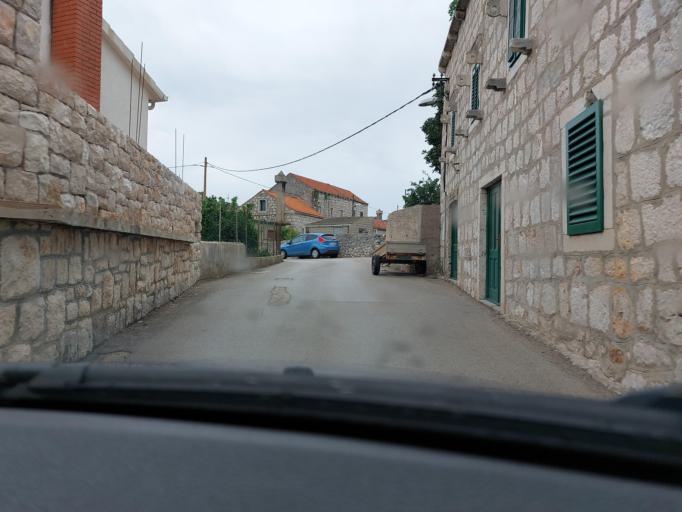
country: HR
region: Dubrovacko-Neretvanska
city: Smokvica
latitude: 42.7663
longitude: 16.9000
